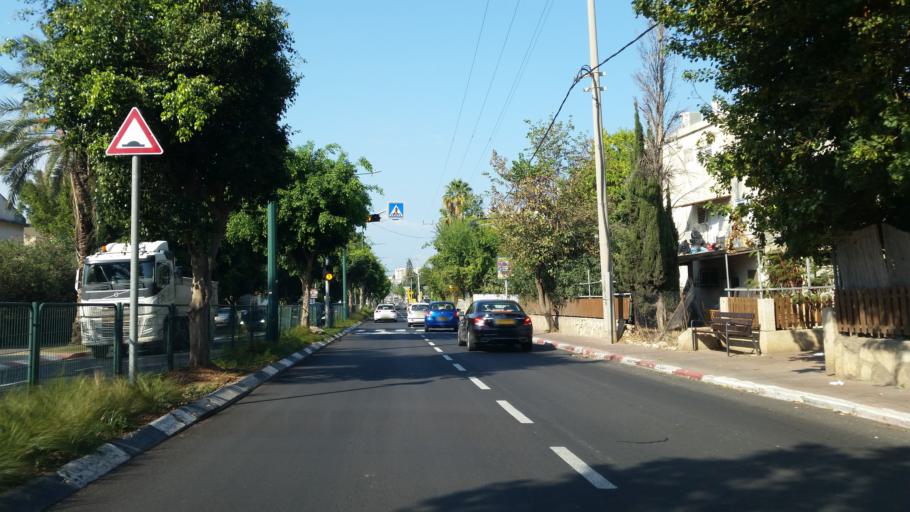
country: IL
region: Tel Aviv
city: Herzliyya
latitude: 32.1627
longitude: 34.8325
